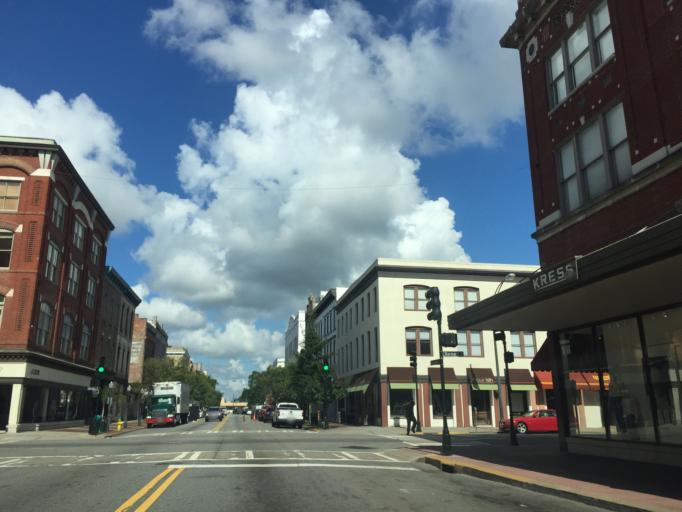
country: US
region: Georgia
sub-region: Chatham County
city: Savannah
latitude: 32.0794
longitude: -81.0939
